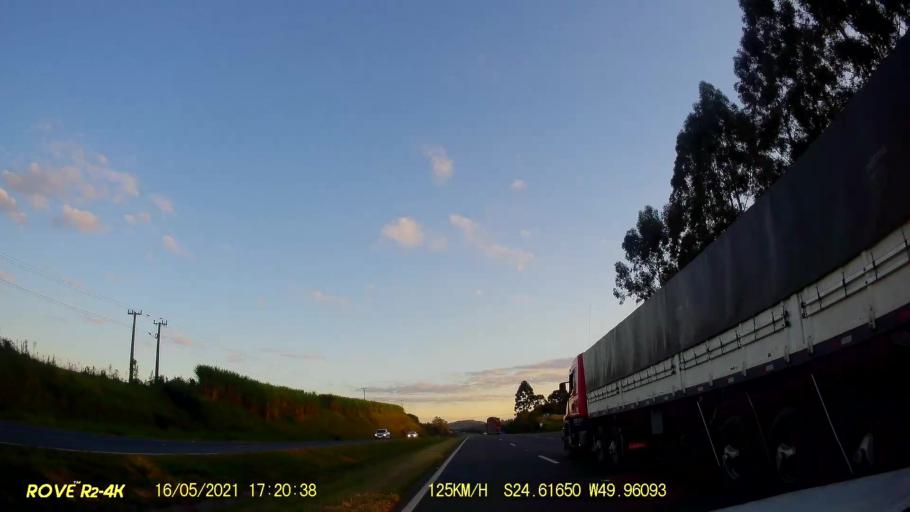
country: BR
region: Parana
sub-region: Pirai Do Sul
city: Pirai do Sul
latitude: -24.6169
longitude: -49.9612
